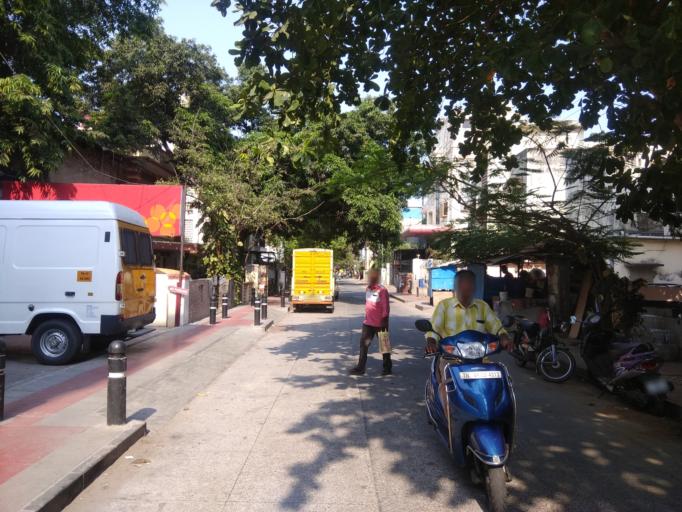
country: IN
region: Tamil Nadu
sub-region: Chennai
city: Chetput
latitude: 13.0429
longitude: 80.2327
